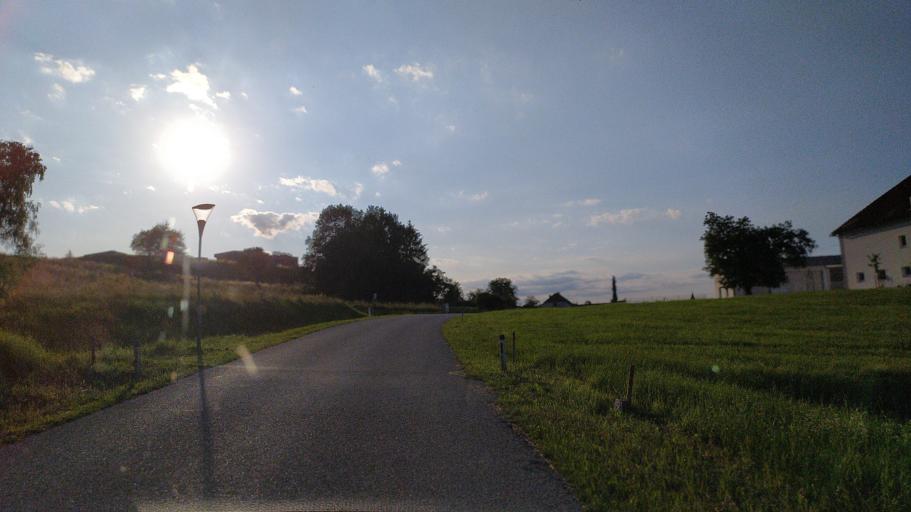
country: AT
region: Lower Austria
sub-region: Politischer Bezirk Amstetten
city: Sankt Valentin
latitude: 48.1989
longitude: 14.5777
